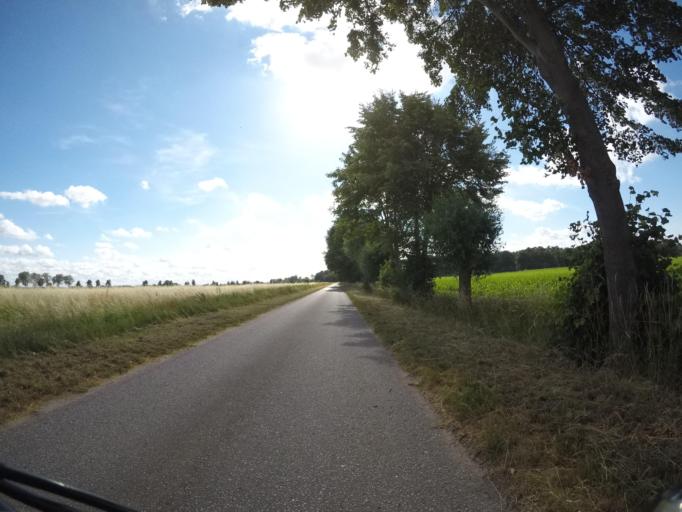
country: DE
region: Lower Saxony
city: Damnatz
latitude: 53.1838
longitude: 11.1325
